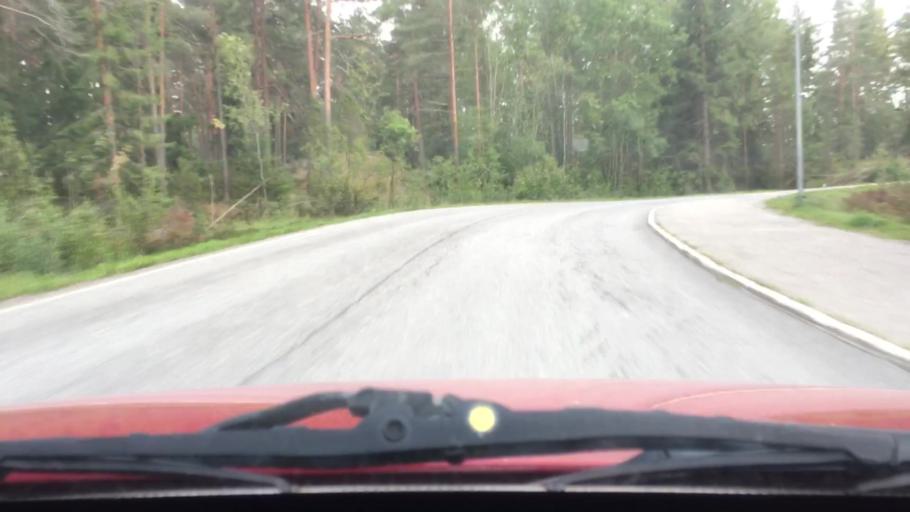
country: FI
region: Varsinais-Suomi
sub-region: Turku
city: Masku
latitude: 60.5526
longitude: 22.1344
